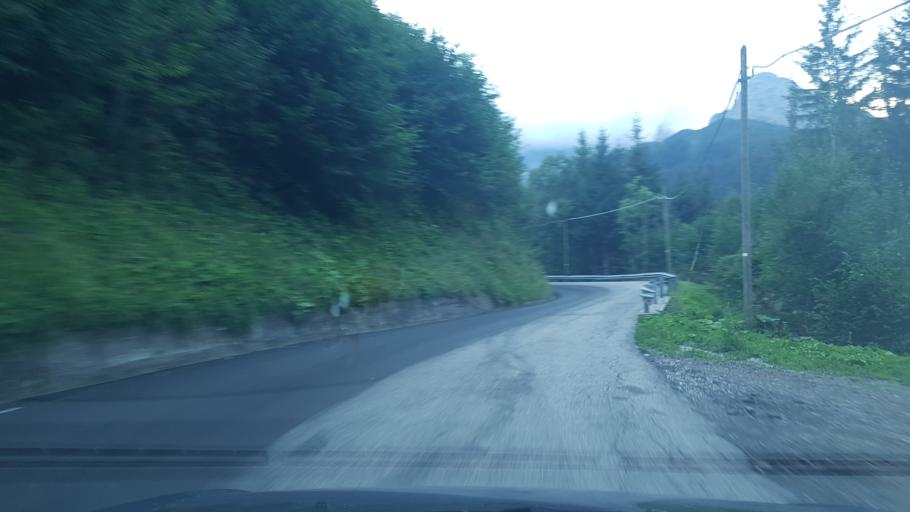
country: IT
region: Friuli Venezia Giulia
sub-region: Provincia di Udine
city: Forni Avoltri
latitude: 46.5850
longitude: 12.7883
